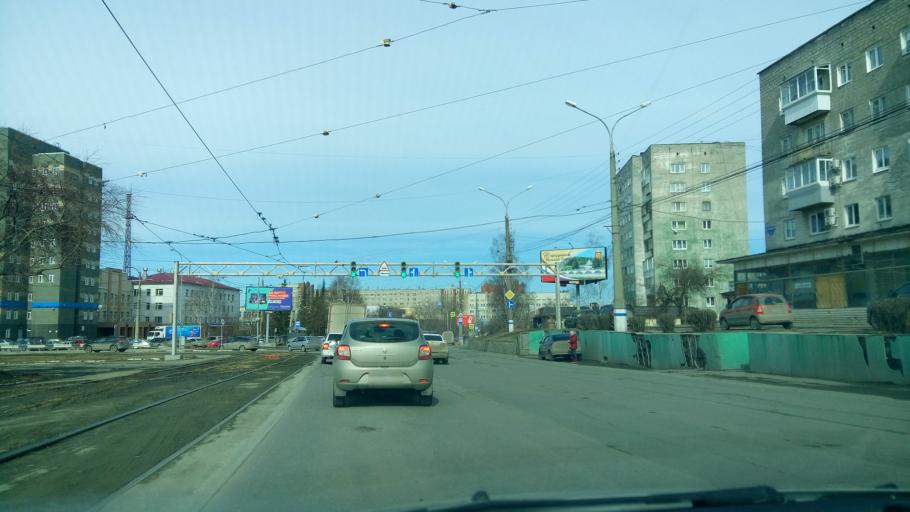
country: RU
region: Sverdlovsk
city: Nizhniy Tagil
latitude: 57.9081
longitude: 59.9477
